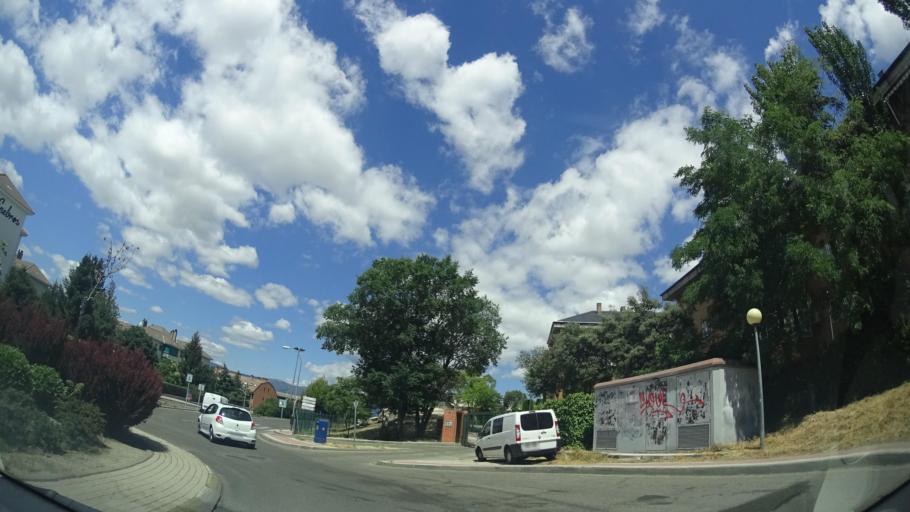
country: ES
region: Madrid
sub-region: Provincia de Madrid
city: Collado-Villalba
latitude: 40.6287
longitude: -3.9993
